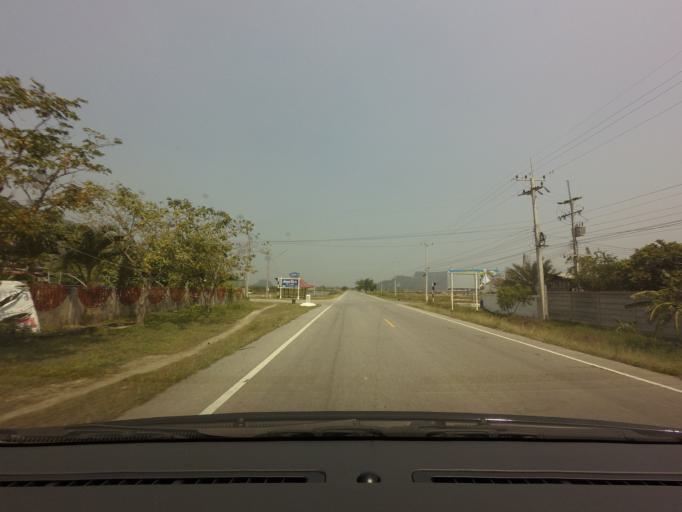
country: TH
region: Prachuap Khiri Khan
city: Sam Roi Yot
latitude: 12.1852
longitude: 99.9762
